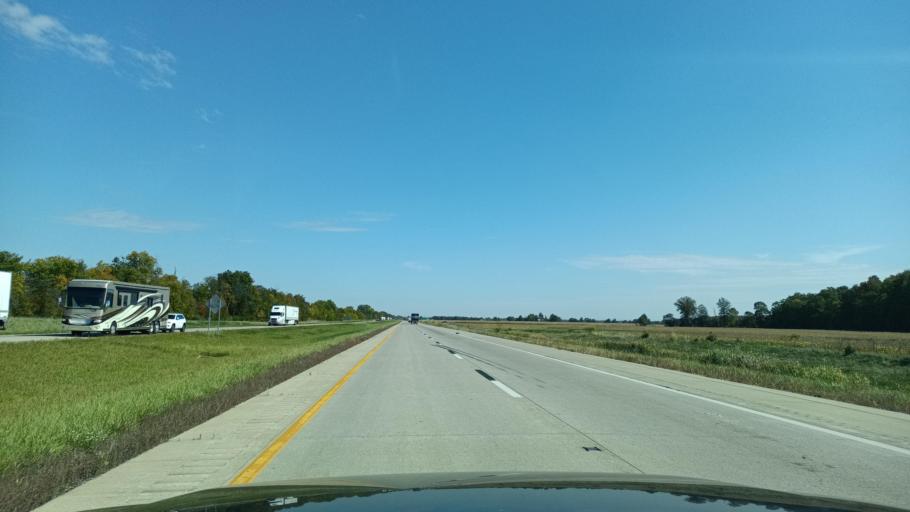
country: US
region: Ohio
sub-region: Paulding County
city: Paulding
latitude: 41.2049
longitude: -84.6474
